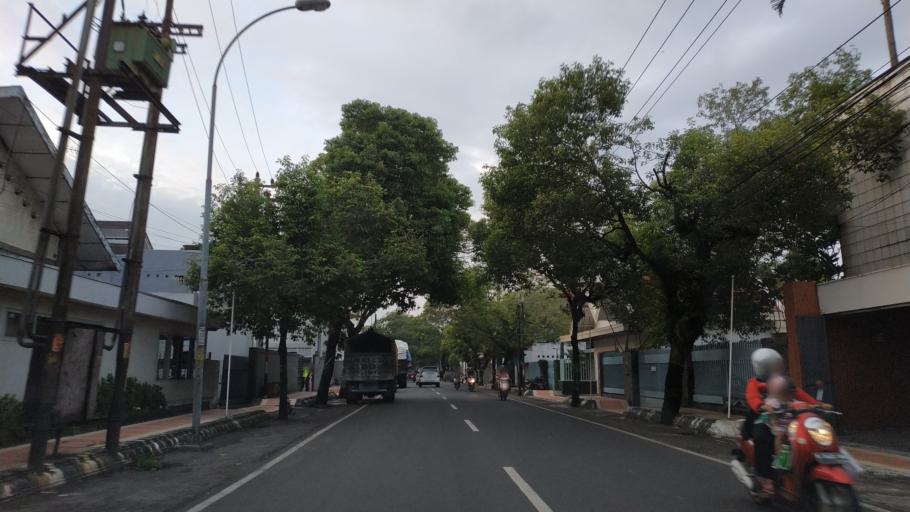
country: ID
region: Central Java
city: Kudus
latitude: -6.8098
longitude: 110.8475
